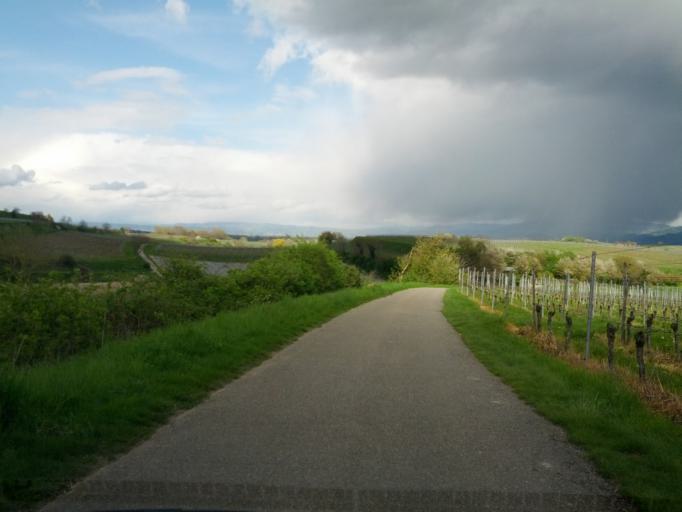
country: DE
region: Baden-Wuerttemberg
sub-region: Freiburg Region
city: Merdingen
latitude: 48.0035
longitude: 7.6924
